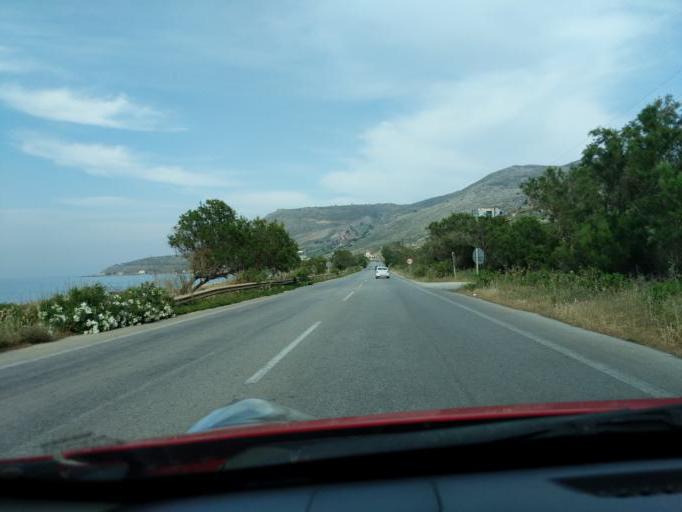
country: GR
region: Crete
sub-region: Nomos Rethymnis
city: Atsipopoulon
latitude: 35.3505
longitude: 24.3501
